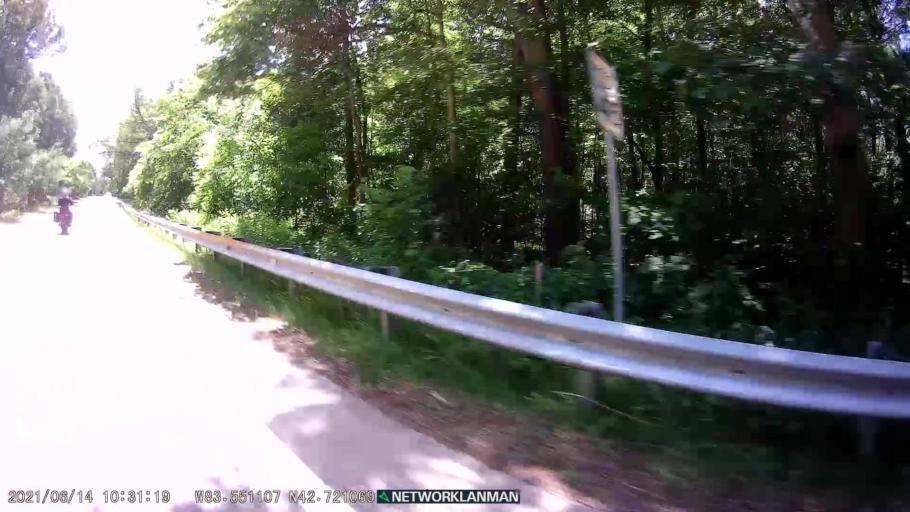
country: US
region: Michigan
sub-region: Oakland County
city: Holly
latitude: 42.7210
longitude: -83.5510
